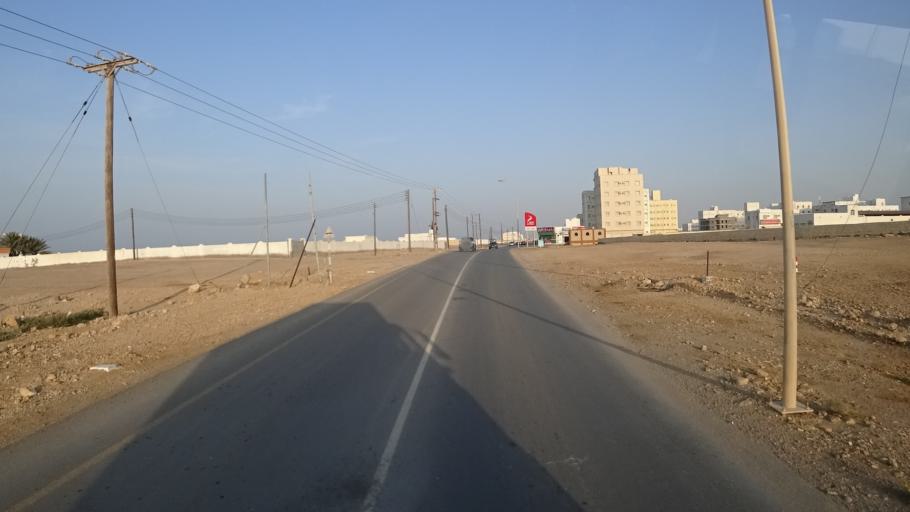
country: OM
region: Ash Sharqiyah
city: Sur
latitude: 22.6094
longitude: 59.4707
